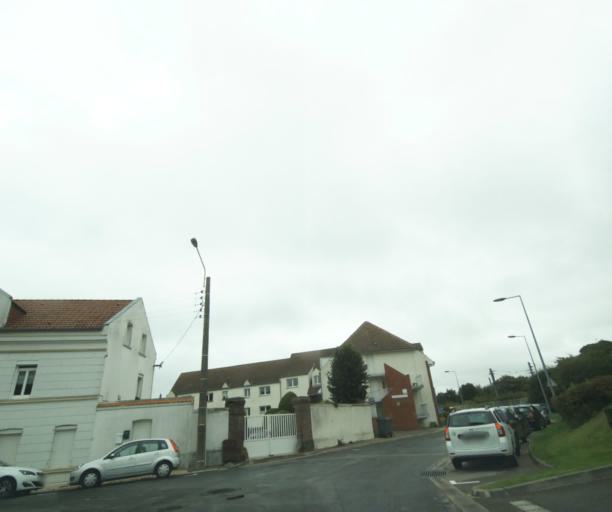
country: FR
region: Nord-Pas-de-Calais
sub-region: Departement du Pas-de-Calais
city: Etaples
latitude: 50.5124
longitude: 1.6434
